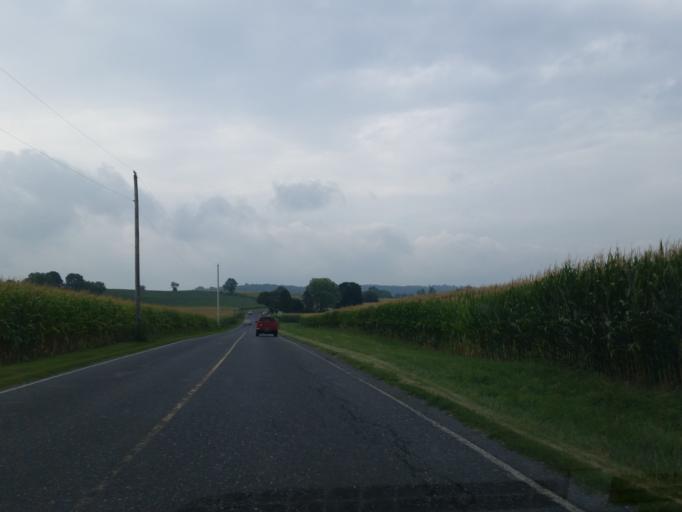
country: US
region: Pennsylvania
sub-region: Lebanon County
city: Richland
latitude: 40.3429
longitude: -76.2623
